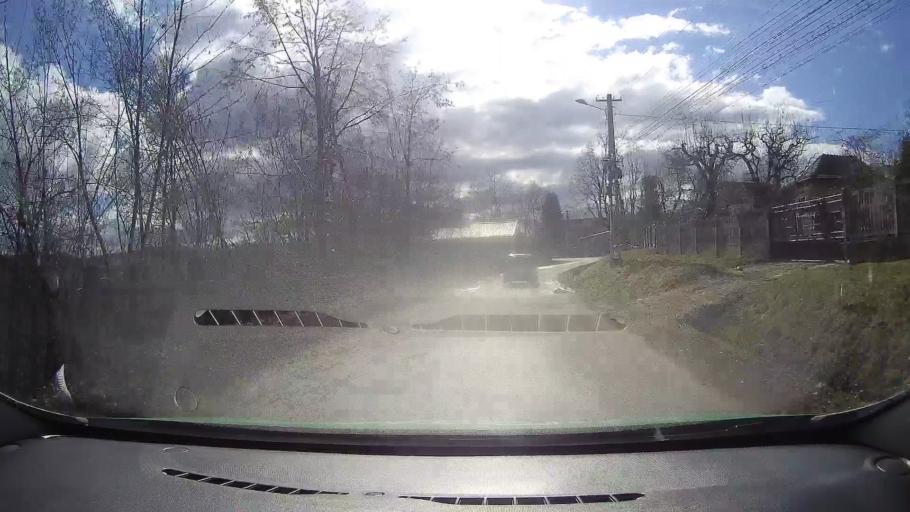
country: RO
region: Dambovita
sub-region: Oras Pucioasa
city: Pucioasa
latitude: 45.0638
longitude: 25.4250
